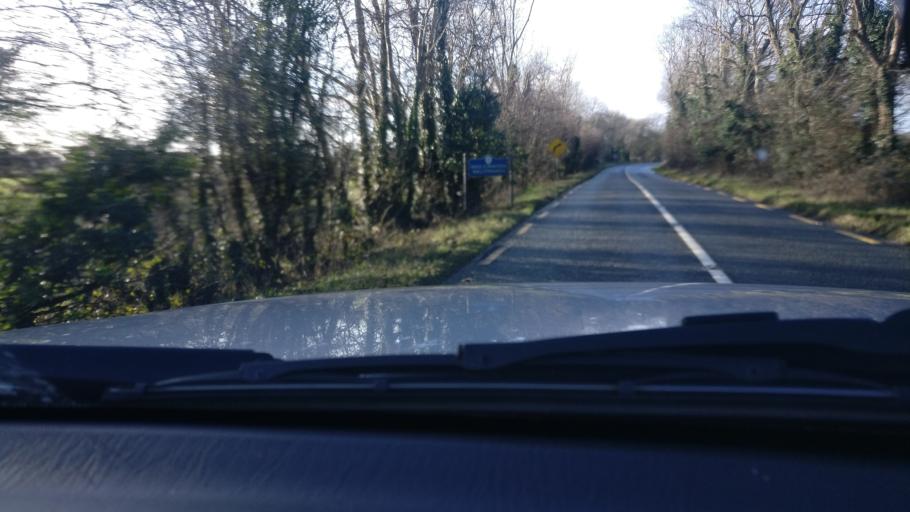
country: IE
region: Leinster
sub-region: An Longfort
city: Ballymahon
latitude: 53.5735
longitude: -7.7467
